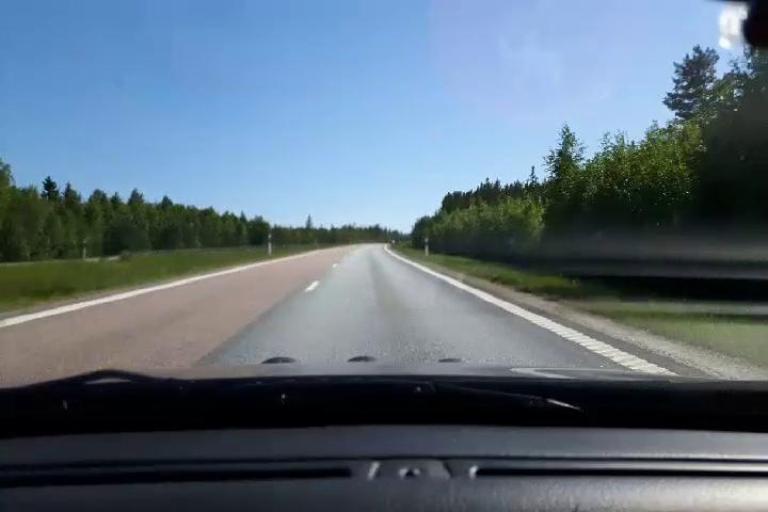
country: SE
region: Gaevleborg
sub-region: Soderhamns Kommun
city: Soderhamn
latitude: 61.4726
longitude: 16.9898
